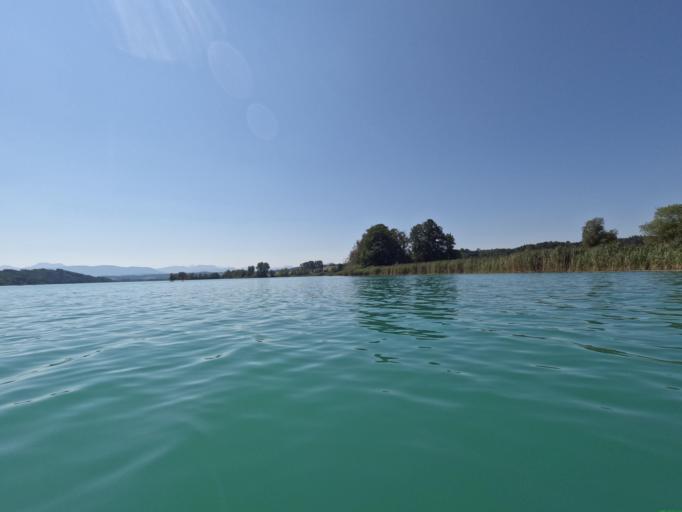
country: DE
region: Bavaria
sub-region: Upper Bavaria
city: Taching am See
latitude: 47.9869
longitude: 12.7424
